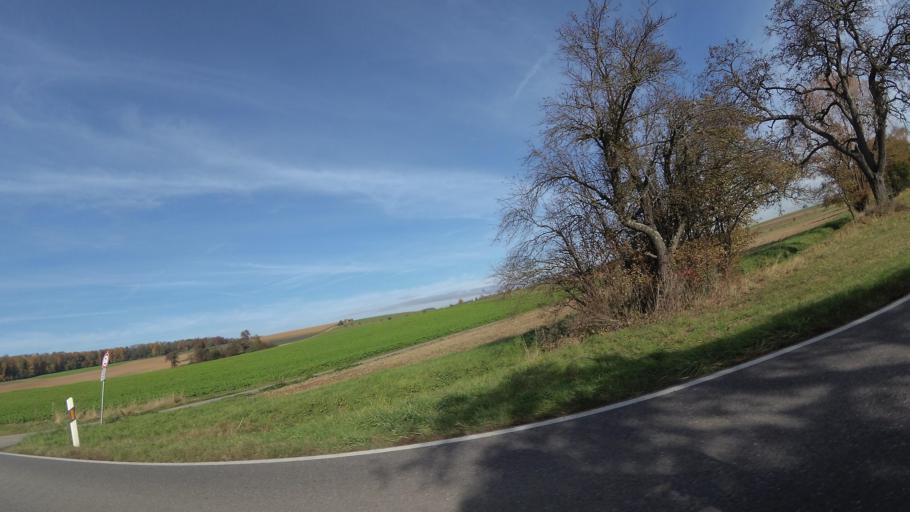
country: DE
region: Baden-Wuerttemberg
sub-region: Regierungsbezirk Stuttgart
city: Gundelsheim
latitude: 49.2680
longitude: 9.1892
